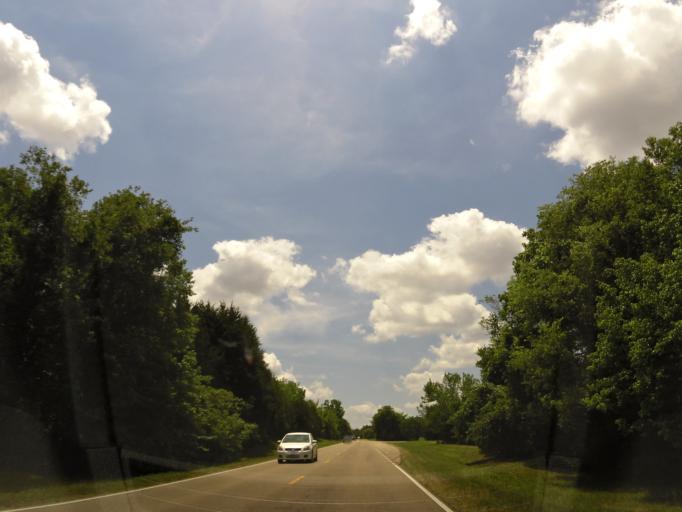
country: US
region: Mississippi
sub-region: Lee County
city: Tupelo
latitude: 34.2759
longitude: -88.7395
